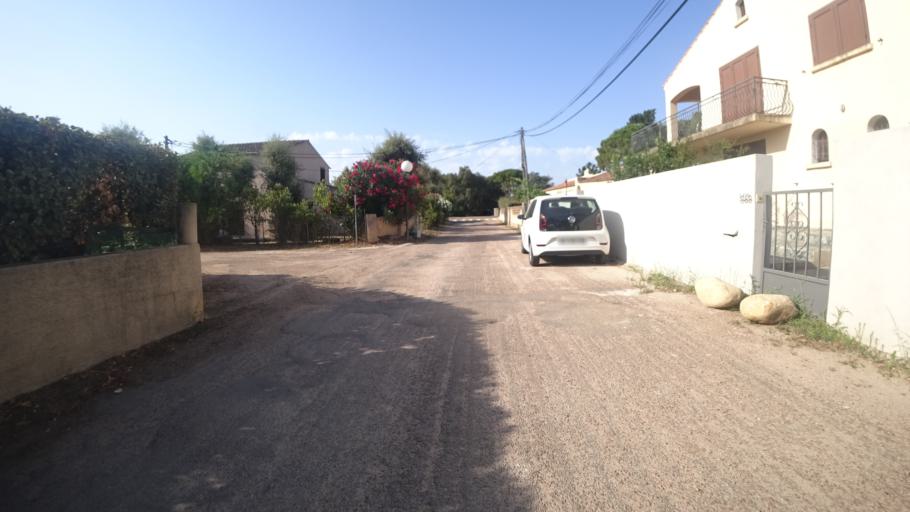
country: FR
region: Corsica
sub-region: Departement de la Corse-du-Sud
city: Porto-Vecchio
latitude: 41.6385
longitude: 9.3405
